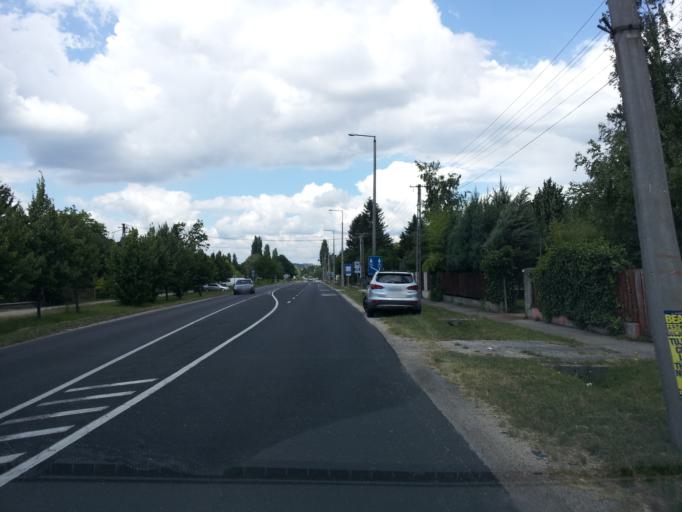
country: HU
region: Veszprem
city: Balatonalmadi
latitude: 47.0492
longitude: 18.0567
